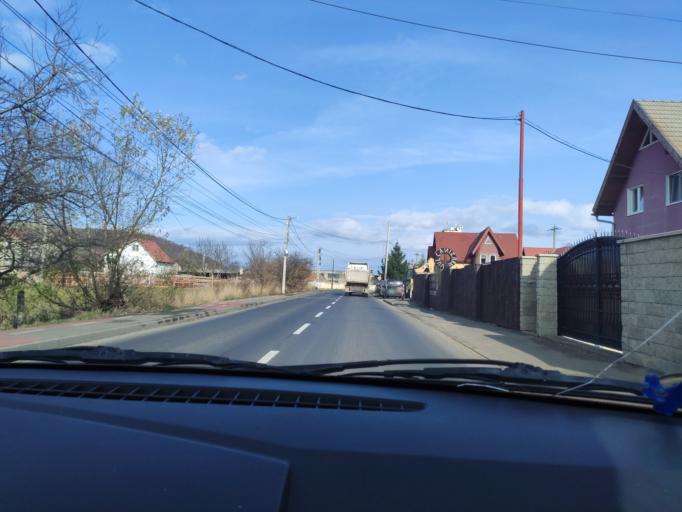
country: RO
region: Brasov
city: Codlea
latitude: 45.7033
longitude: 25.4565
